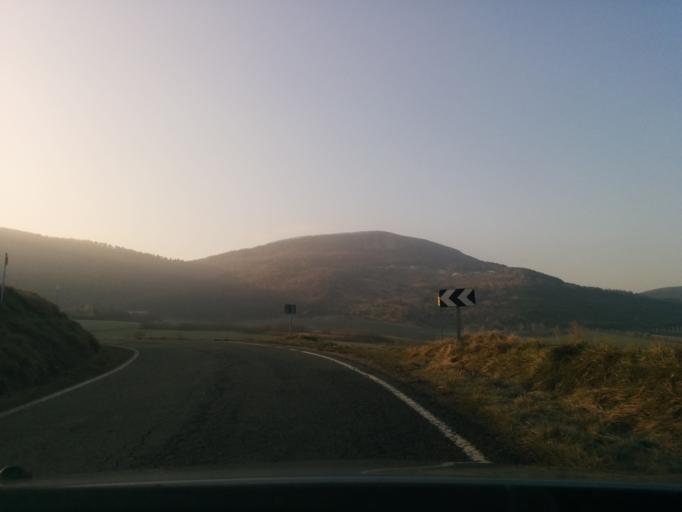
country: ES
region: Navarre
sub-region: Provincia de Navarra
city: Elorz
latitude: 42.7676
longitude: -1.5341
